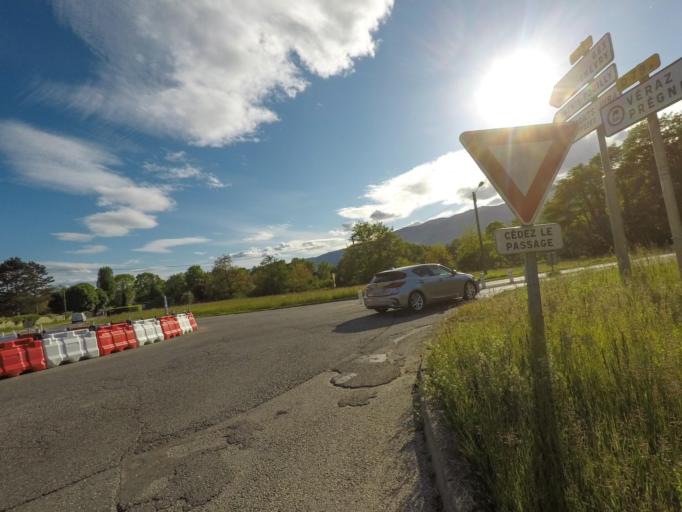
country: FR
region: Rhone-Alpes
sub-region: Departement de l'Ain
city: Chevry
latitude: 46.2574
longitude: 6.0389
